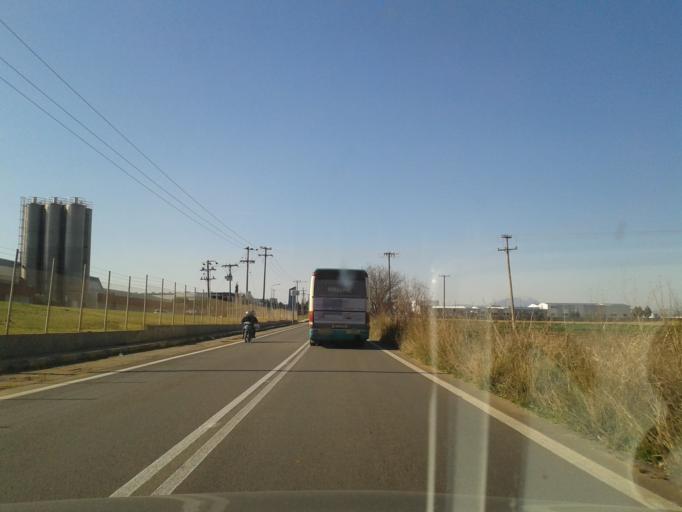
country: GR
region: Central Greece
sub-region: Nomos Voiotias
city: Thivai
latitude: 38.3507
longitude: 23.3815
